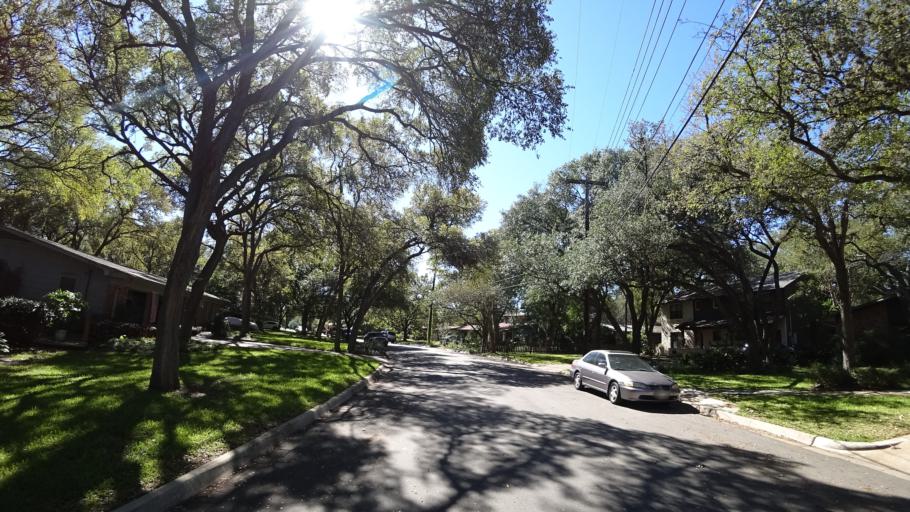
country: US
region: Texas
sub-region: Travis County
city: Austin
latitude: 30.3288
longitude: -97.7477
